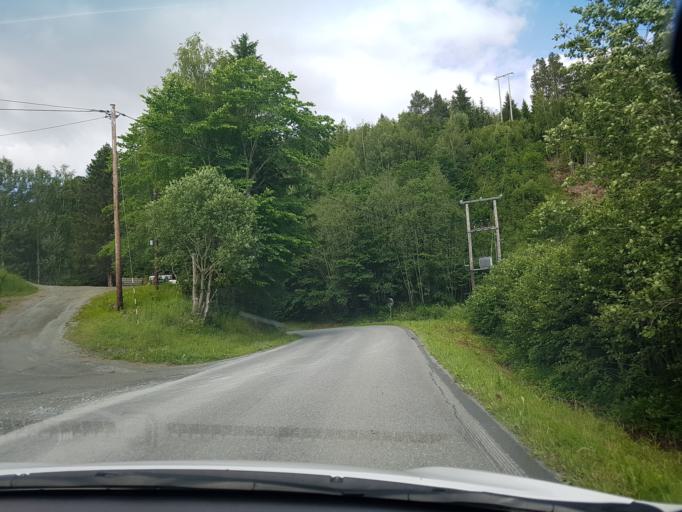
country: NO
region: Nord-Trondelag
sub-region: Stjordal
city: Stjordalshalsen
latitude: 63.5969
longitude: 10.9701
